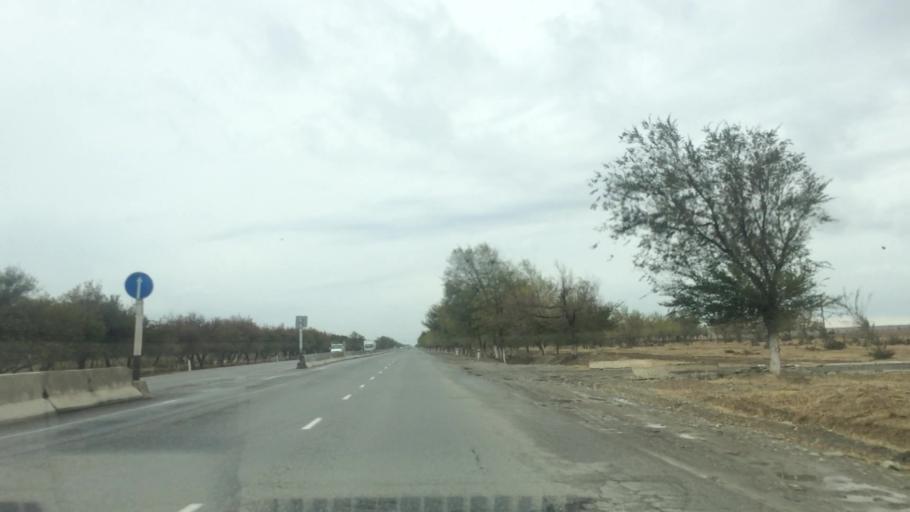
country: UZ
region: Samarqand
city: Bulung'ur
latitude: 39.8359
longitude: 67.4244
